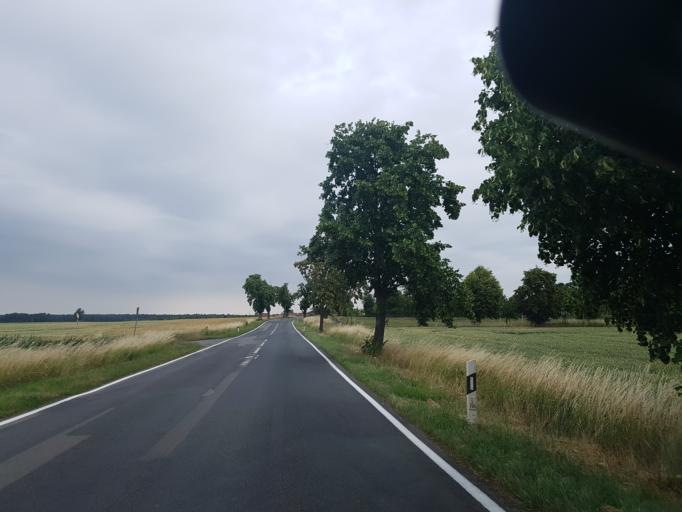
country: DE
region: Brandenburg
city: Lebusa
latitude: 51.7932
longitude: 13.4105
